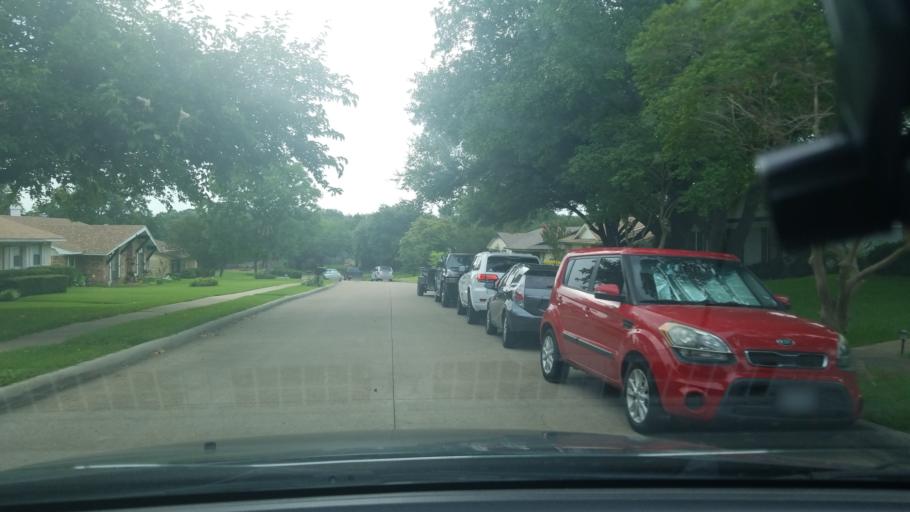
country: US
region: Texas
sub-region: Dallas County
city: Mesquite
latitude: 32.7833
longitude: -96.6416
